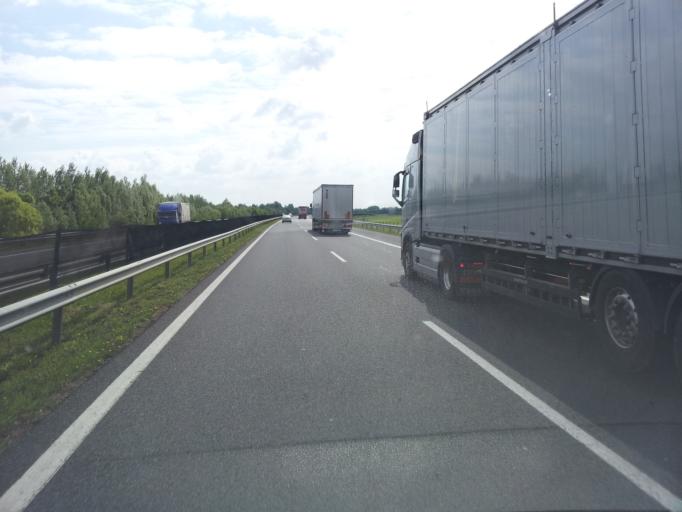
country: HU
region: Borsod-Abauj-Zemplen
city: Hejobaba
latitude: 47.8735
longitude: 20.9524
